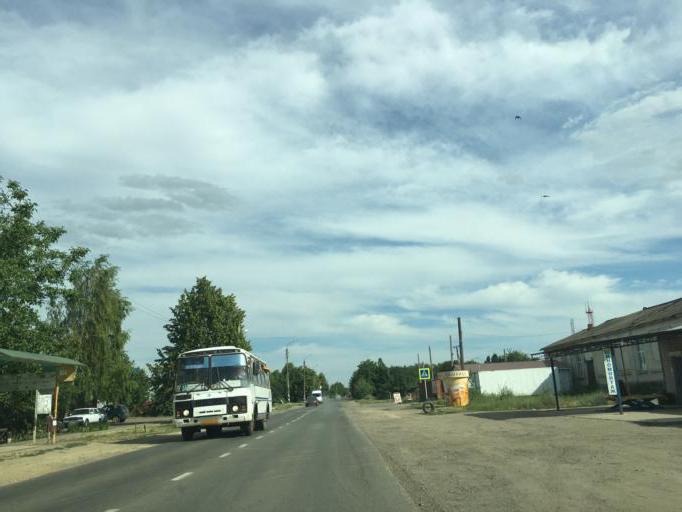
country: RU
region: Krasnodarskiy
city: Kushchevskaya
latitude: 46.5467
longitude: 39.6193
